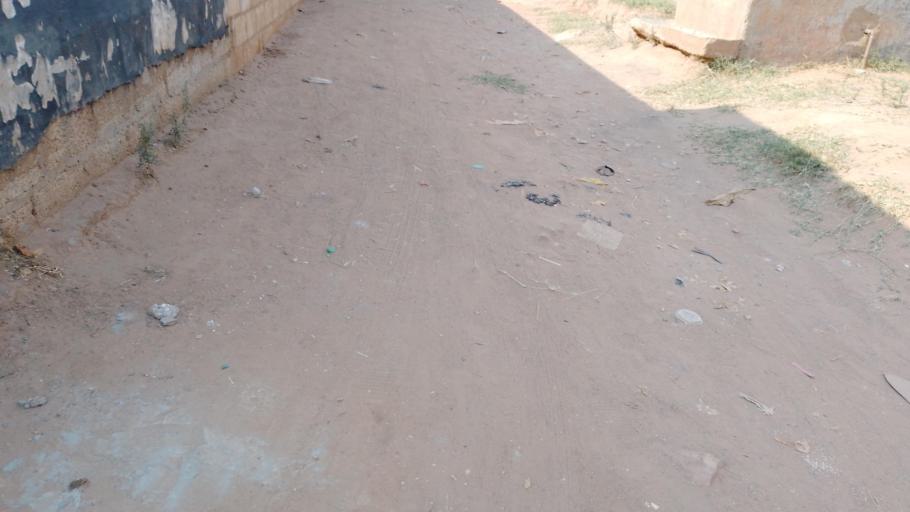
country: ZM
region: Lusaka
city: Lusaka
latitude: -15.3961
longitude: 28.3712
